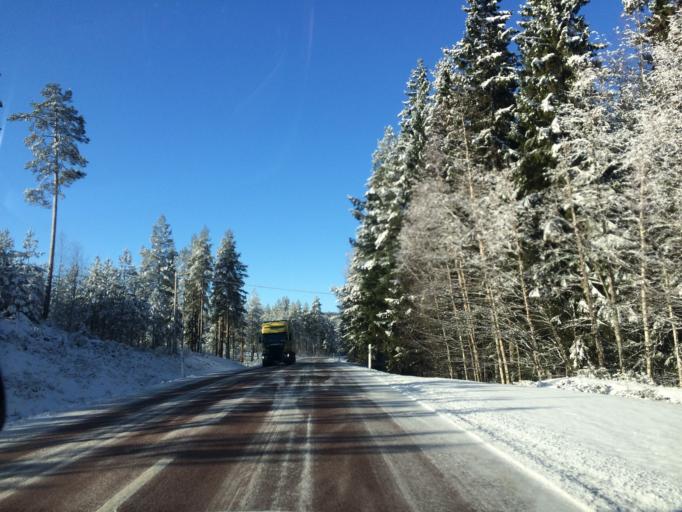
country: SE
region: Dalarna
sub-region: Mora Kommun
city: Mora
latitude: 60.8625
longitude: 14.3441
